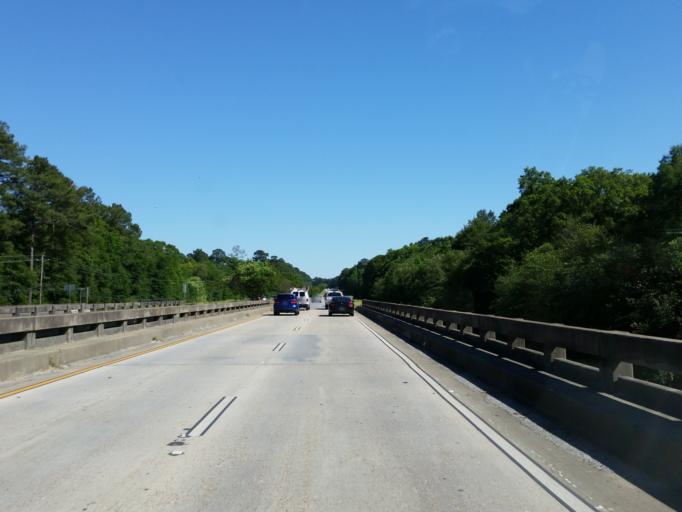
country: US
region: Georgia
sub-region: Lowndes County
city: Remerton
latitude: 30.8929
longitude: -83.3192
